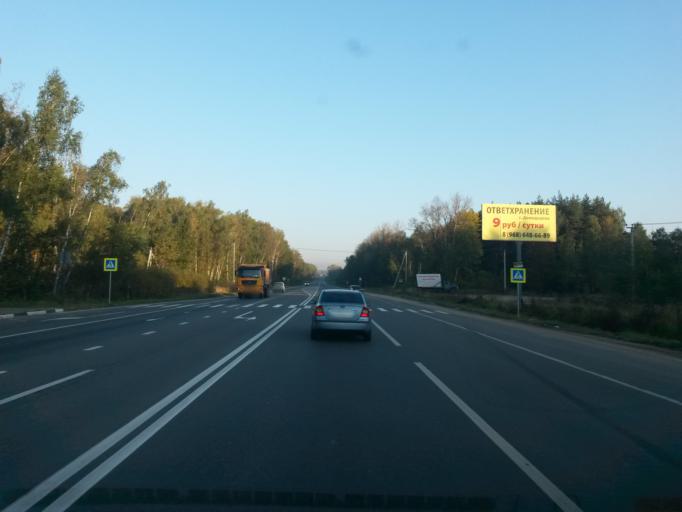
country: RU
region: Moskovskaya
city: Barybino
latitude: 55.2333
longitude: 37.8646
